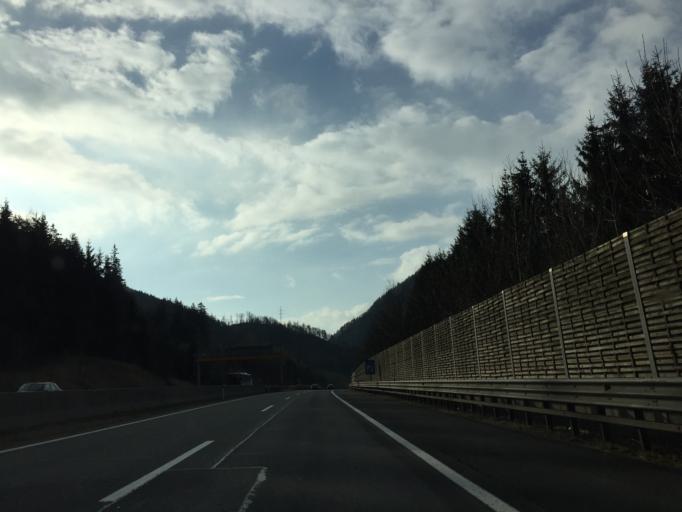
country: AT
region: Salzburg
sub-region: Politischer Bezirk Sankt Johann im Pongau
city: Werfen
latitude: 47.4996
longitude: 13.1798
